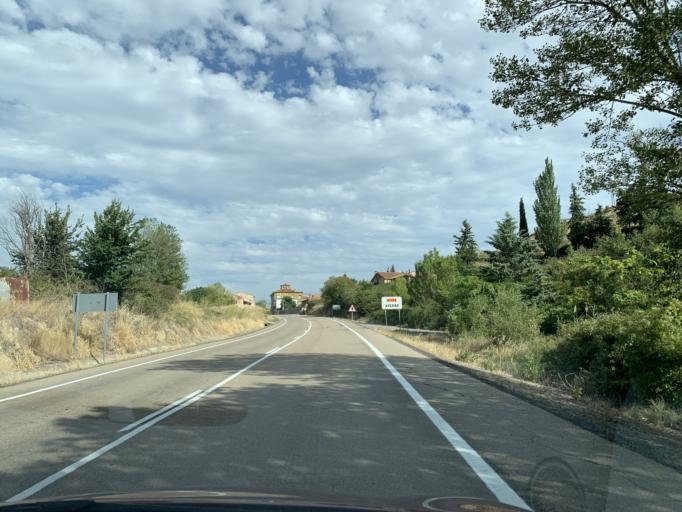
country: ES
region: Aragon
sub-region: Provincia de Huesca
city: Ayerbe
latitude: 42.2797
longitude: -0.6939
